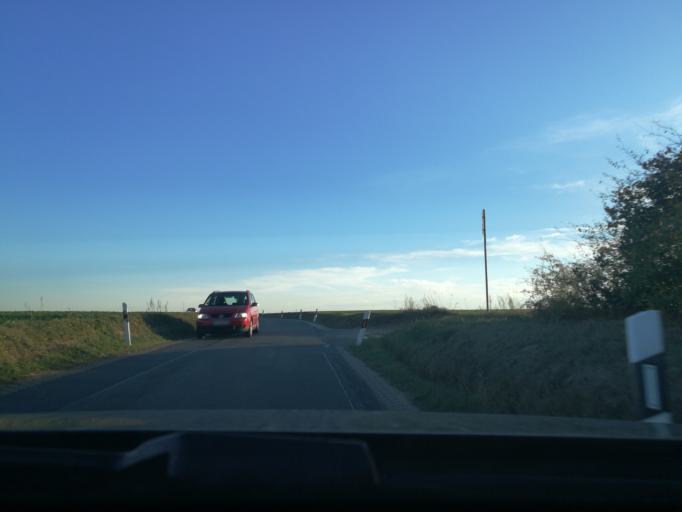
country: DE
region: Bavaria
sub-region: Regierungsbezirk Mittelfranken
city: Obermichelbach
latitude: 49.5018
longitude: 10.9346
